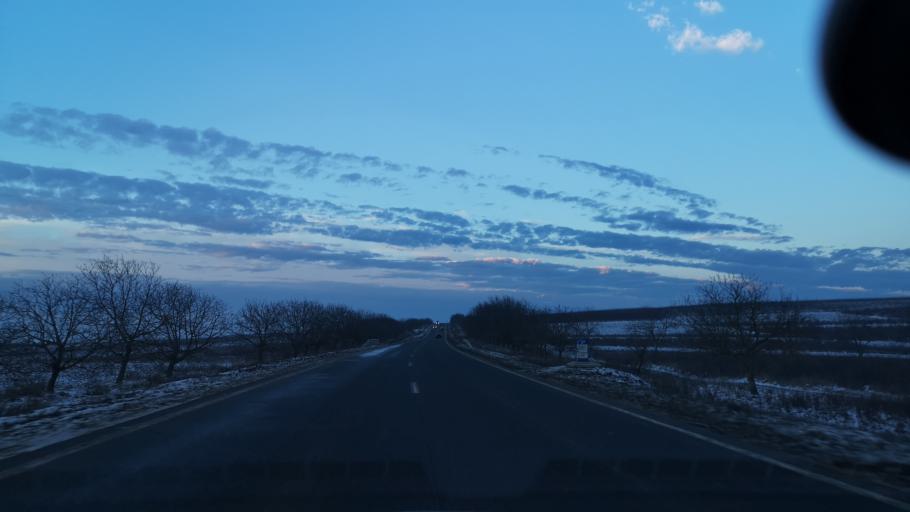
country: MD
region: Rezina
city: Saharna
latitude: 47.6094
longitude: 28.8304
